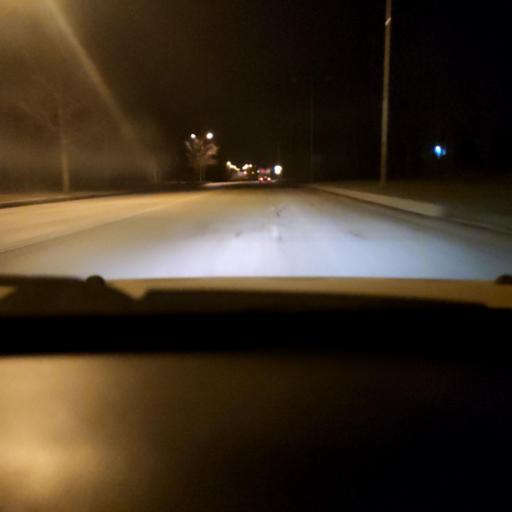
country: RU
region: Perm
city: Perm
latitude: 58.1015
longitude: 56.3902
